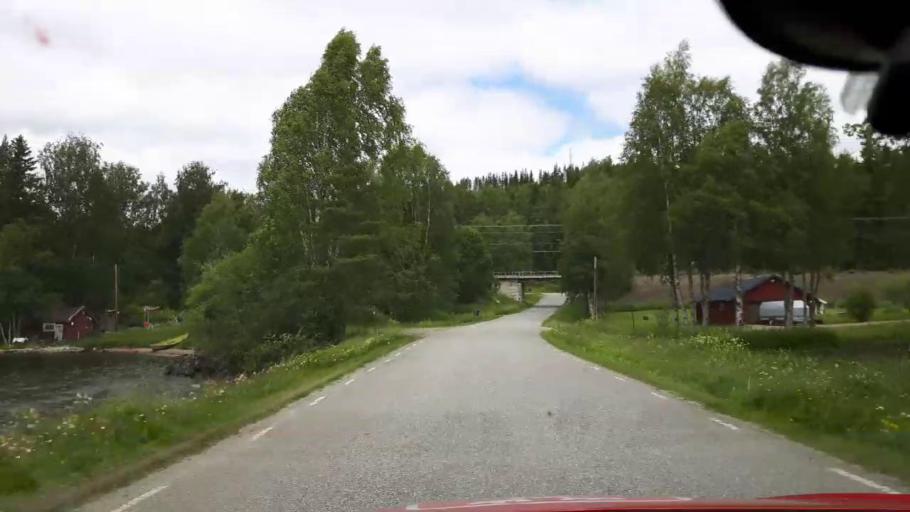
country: SE
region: Jaemtland
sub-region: Braecke Kommun
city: Braecke
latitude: 62.8875
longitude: 15.2730
